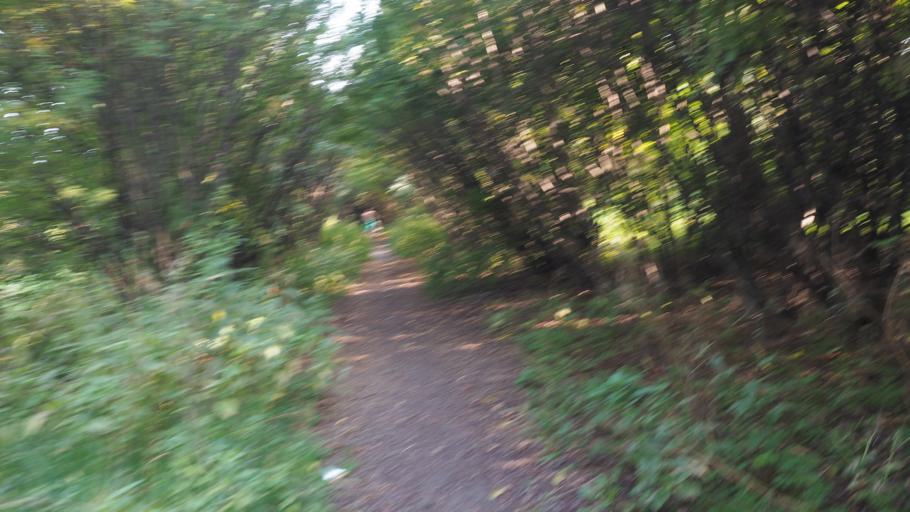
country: RU
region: Moscow
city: Orekhovo-Borisovo Severnoye
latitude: 55.6187
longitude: 37.6917
